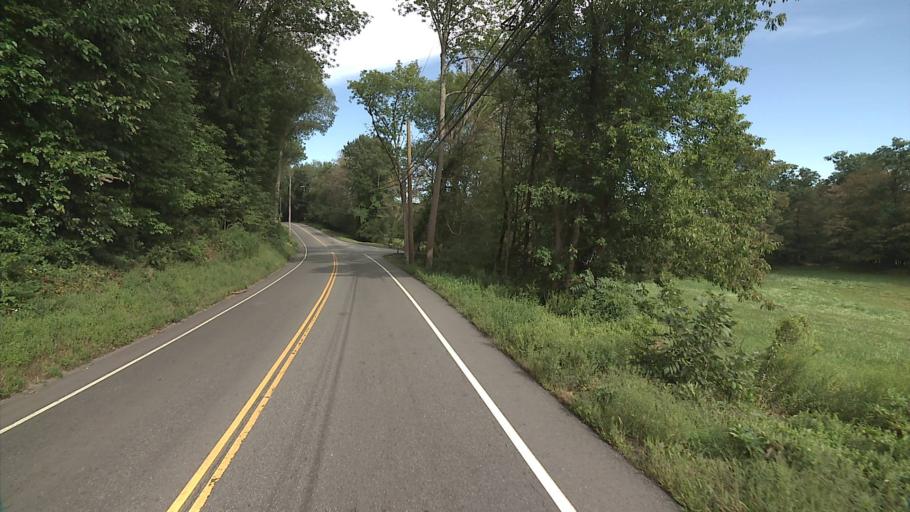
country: US
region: Connecticut
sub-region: New London County
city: Baltic
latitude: 41.6061
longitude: -72.1374
